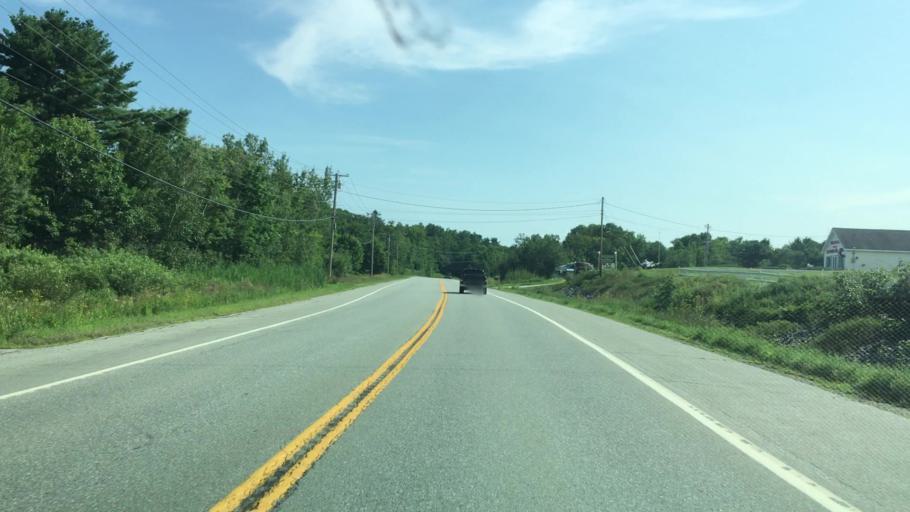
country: US
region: Maine
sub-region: Waldo County
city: Frankfort
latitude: 44.6164
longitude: -68.8698
